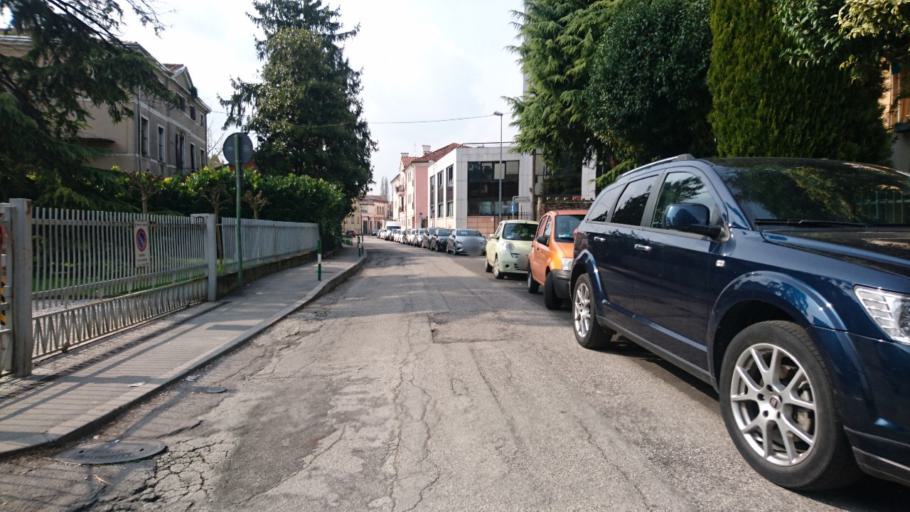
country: IT
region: Veneto
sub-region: Provincia di Padova
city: Noventa
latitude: 45.4232
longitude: 11.9454
